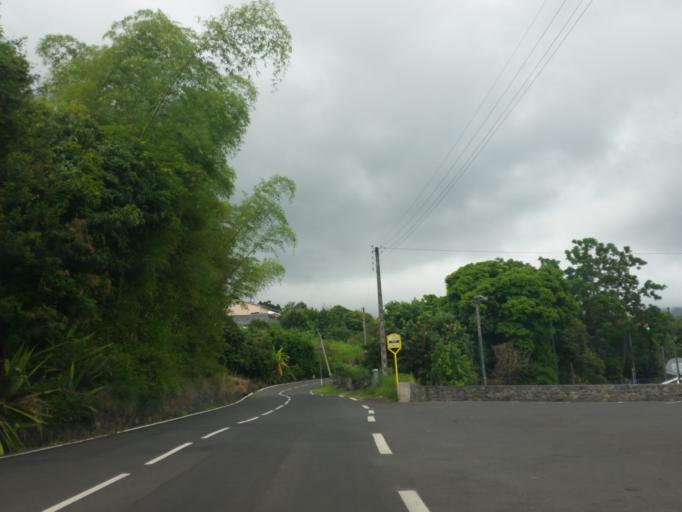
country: RE
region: Reunion
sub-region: Reunion
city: L'Entre-Deux
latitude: -21.2468
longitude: 55.4794
